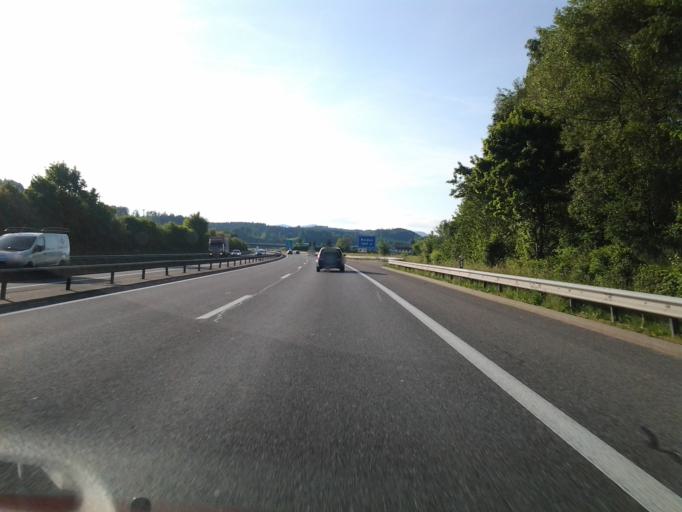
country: CH
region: Lucerne
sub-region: Willisau District
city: Reiden
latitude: 47.2336
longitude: 7.9680
